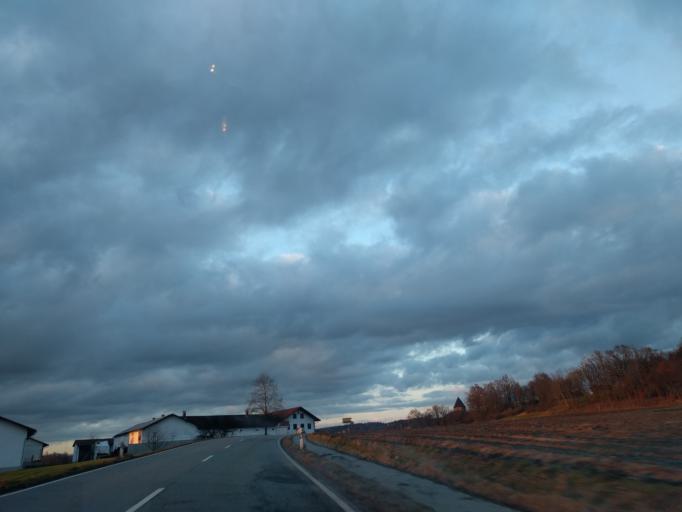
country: DE
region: Bavaria
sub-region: Lower Bavaria
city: Hofkirchen
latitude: 48.6820
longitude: 13.1170
